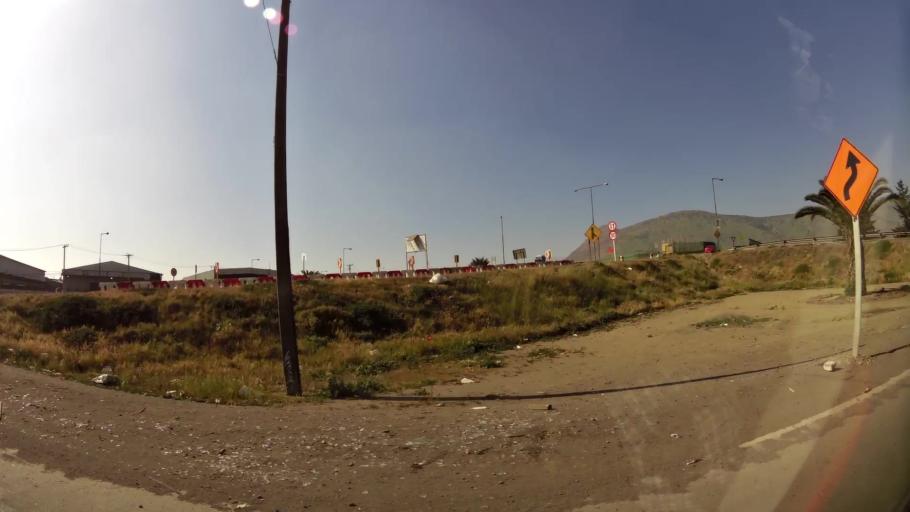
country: CL
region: Santiago Metropolitan
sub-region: Provincia de Chacabuco
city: Chicureo Abajo
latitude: -33.3347
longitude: -70.7158
